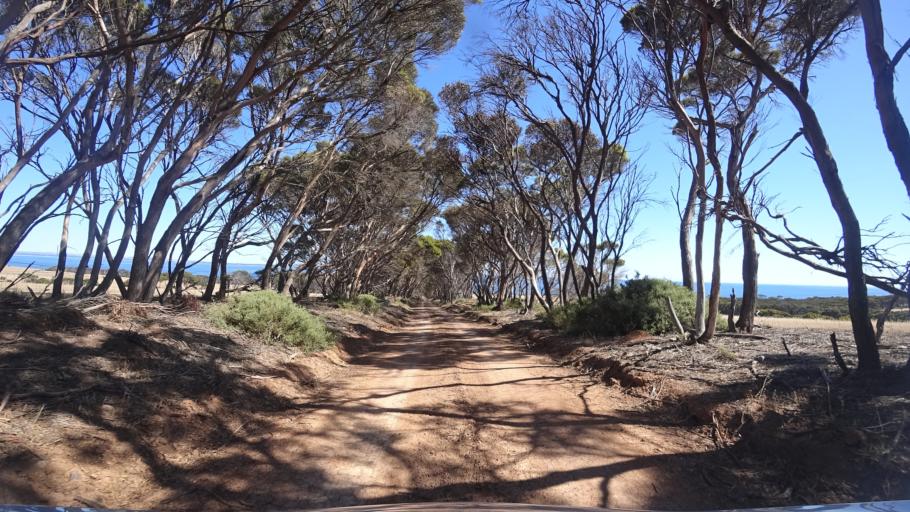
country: AU
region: South Australia
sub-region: Kangaroo Island
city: Kingscote
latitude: -35.7426
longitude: 137.7217
